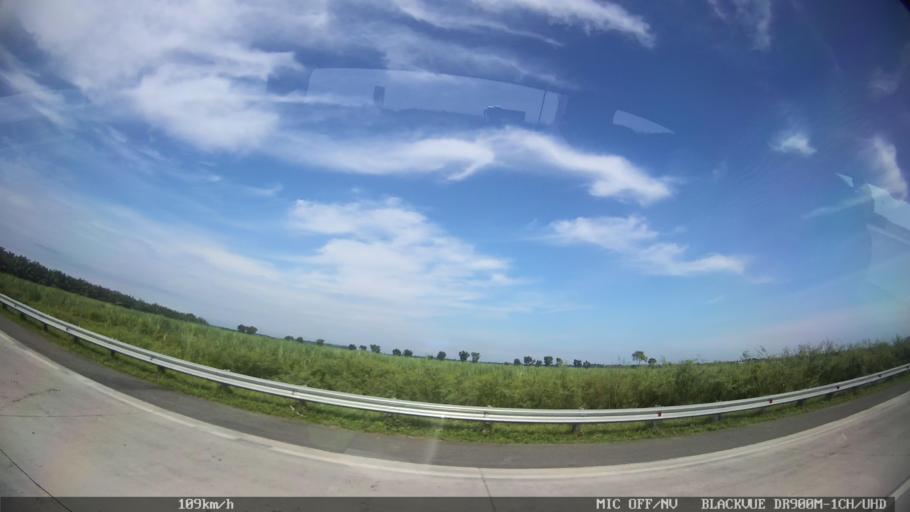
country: ID
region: North Sumatra
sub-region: Kabupaten Langkat
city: Stabat
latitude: 3.6914
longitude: 98.5400
